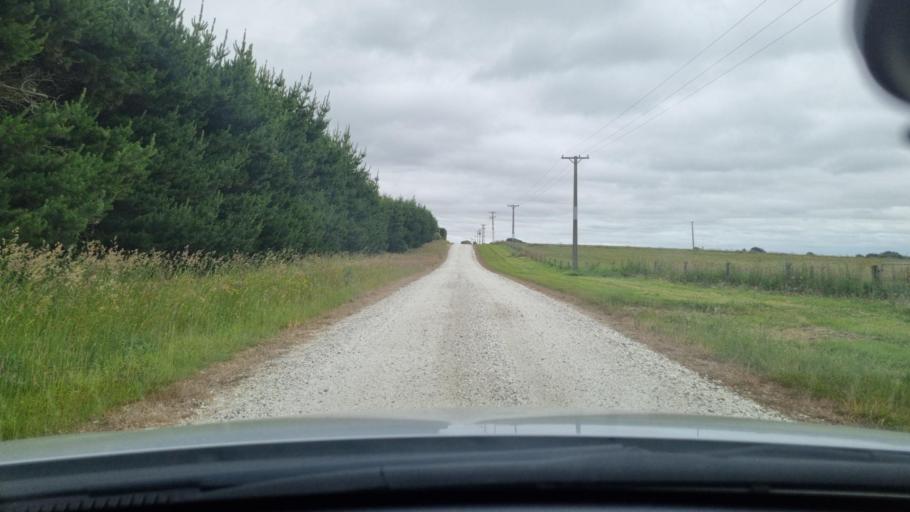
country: NZ
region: Southland
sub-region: Invercargill City
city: Invercargill
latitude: -46.3667
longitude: 168.3792
